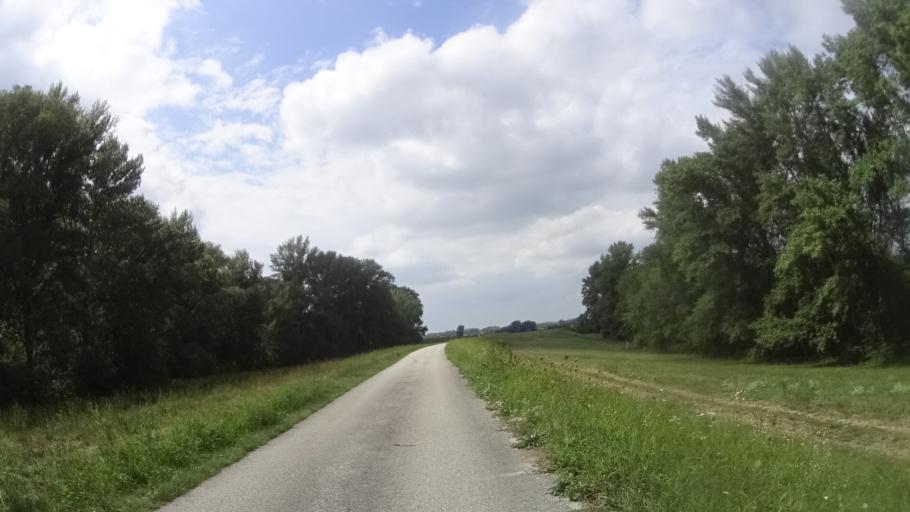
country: SK
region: Trnavsky
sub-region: Okres Dunajska Streda
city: Velky Meder
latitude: 47.7926
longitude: 17.6867
